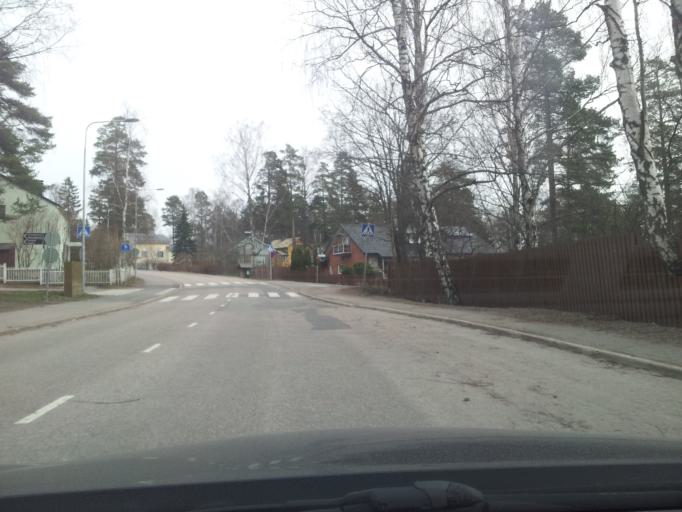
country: FI
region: Uusimaa
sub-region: Helsinki
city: Kilo
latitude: 60.2021
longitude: 24.8047
